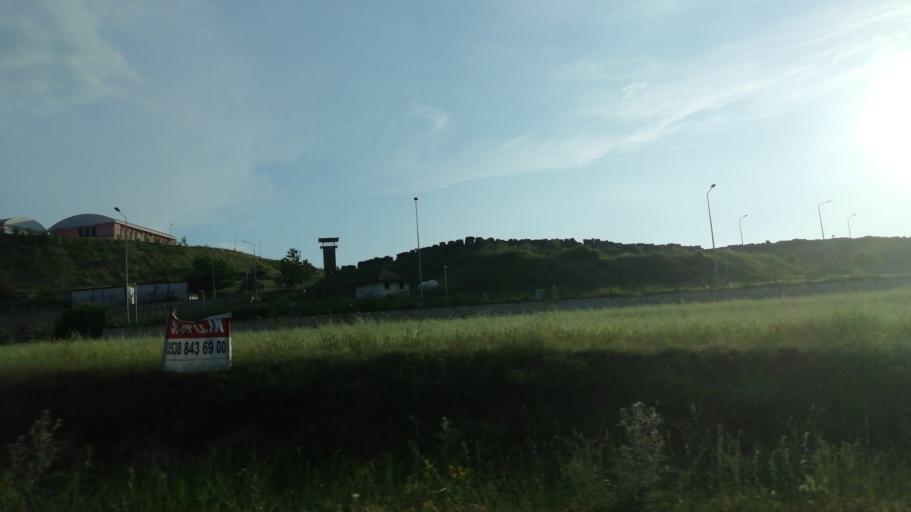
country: TR
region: Karabuk
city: Karabuk
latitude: 41.1377
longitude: 32.6316
